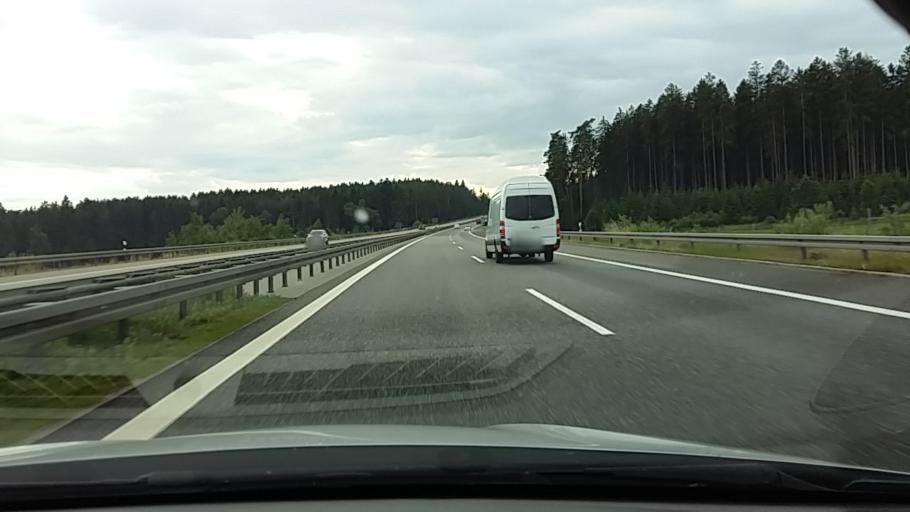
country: DE
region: Bavaria
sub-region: Upper Palatinate
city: Moosbach
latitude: 49.6113
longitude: 12.3947
